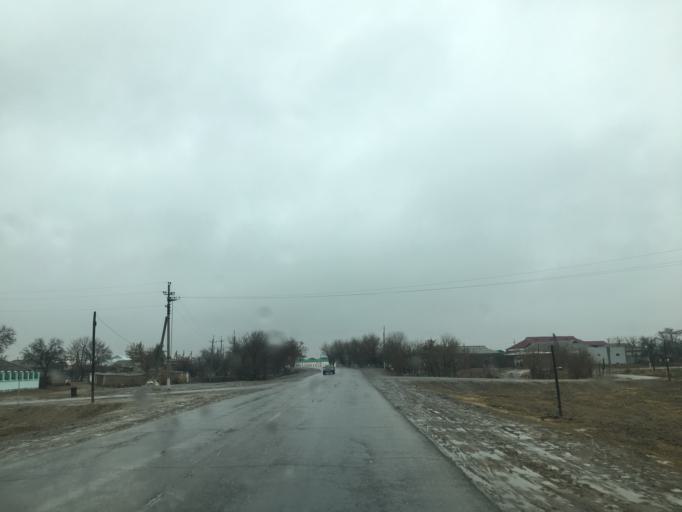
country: TM
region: Mary
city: Yoloeten
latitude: 37.2960
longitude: 62.3326
